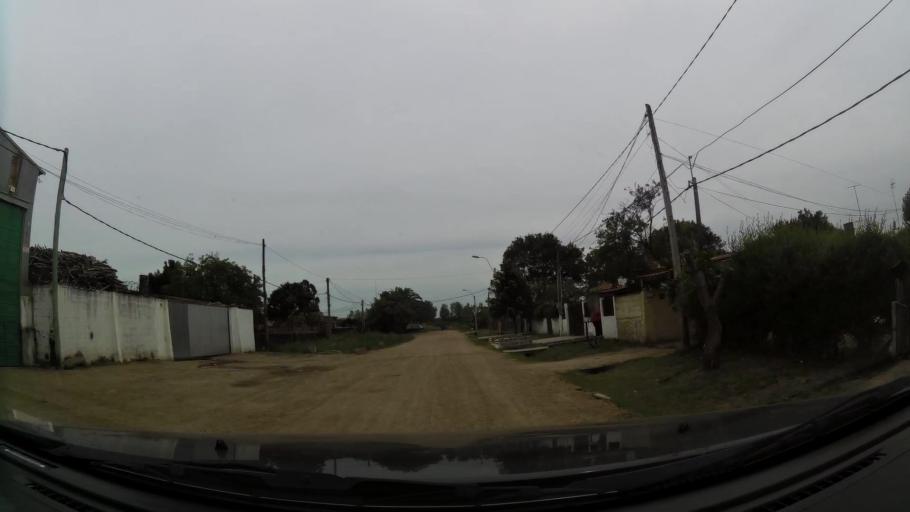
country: UY
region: Canelones
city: La Paz
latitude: -34.7459
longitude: -56.2229
